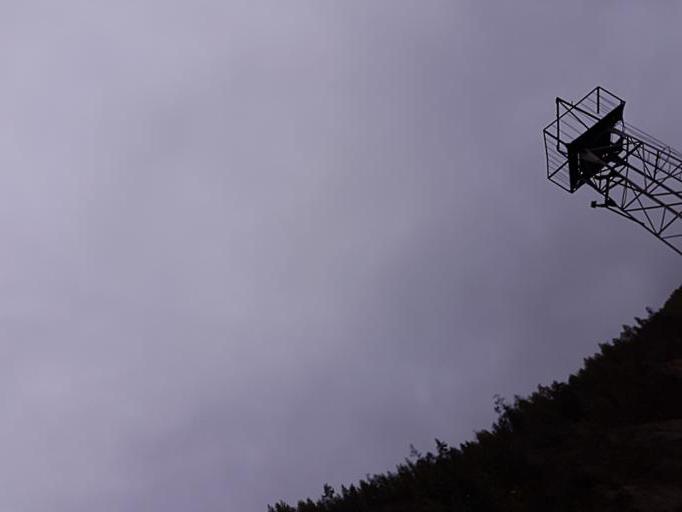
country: RU
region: Sakha
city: Kangalassy
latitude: 62.3654
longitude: 130.0228
